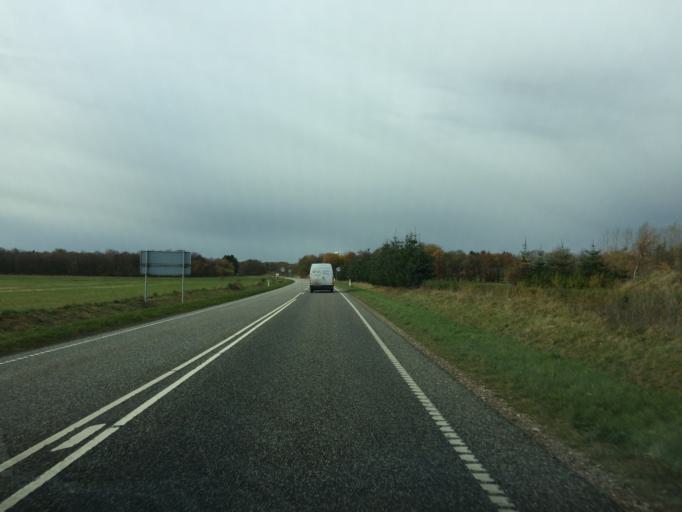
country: DK
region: Central Jutland
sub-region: Herning Kommune
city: Vildbjerg
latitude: 56.1892
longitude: 8.7891
